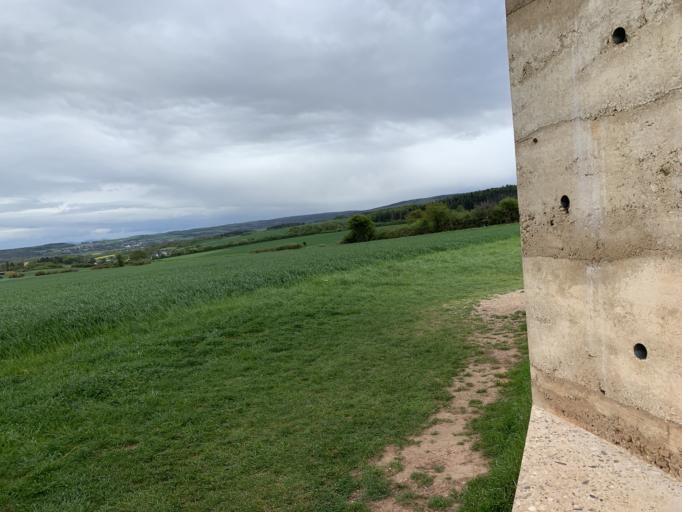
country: DE
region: North Rhine-Westphalia
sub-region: Regierungsbezirk Koln
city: Bad Munstereifel
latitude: 50.5925
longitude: 6.7273
